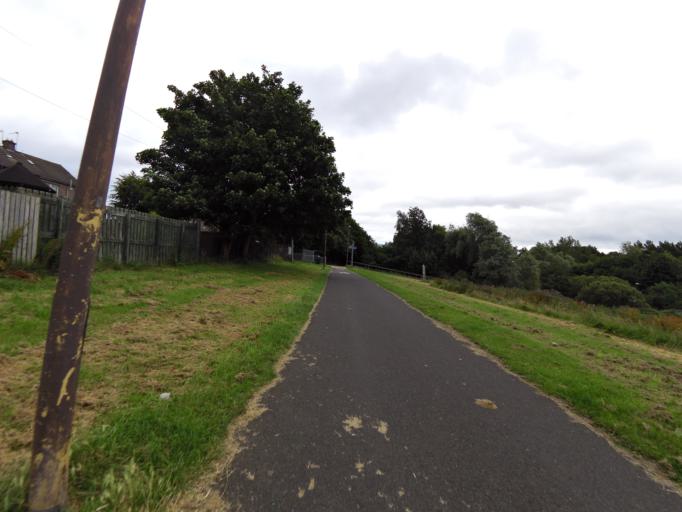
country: GB
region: Scotland
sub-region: West Lothian
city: Seafield
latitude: 55.9406
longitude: -3.1064
